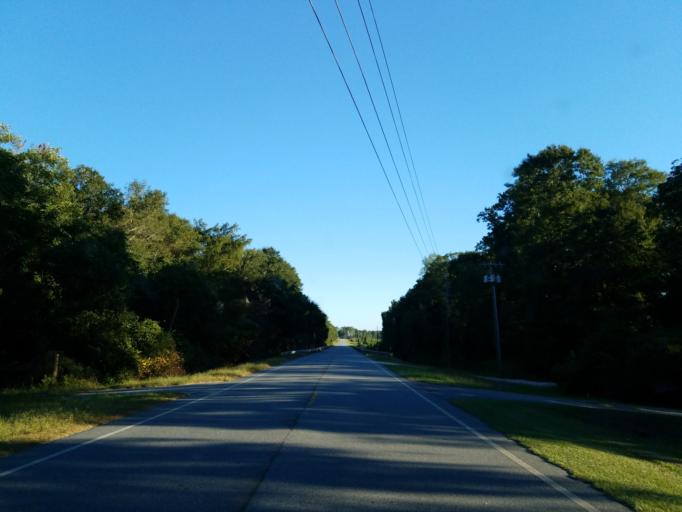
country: US
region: Georgia
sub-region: Worth County
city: Sylvester
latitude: 31.6891
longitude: -83.8824
